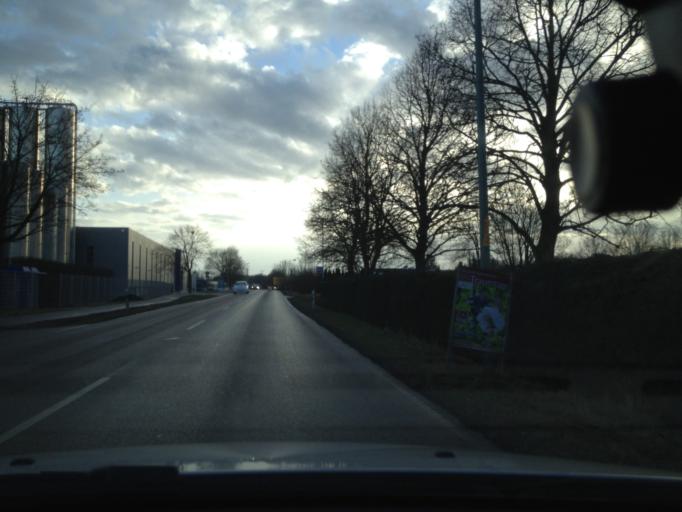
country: DE
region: Bavaria
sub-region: Swabia
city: Schwabmunchen
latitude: 48.1690
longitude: 10.7564
